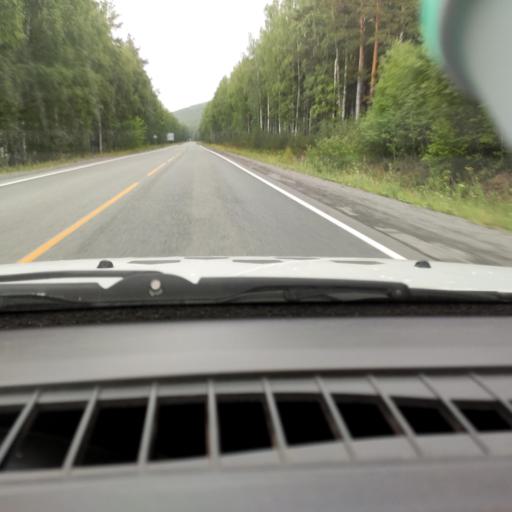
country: RU
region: Chelyabinsk
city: Karabash
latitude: 55.3191
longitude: 60.2175
